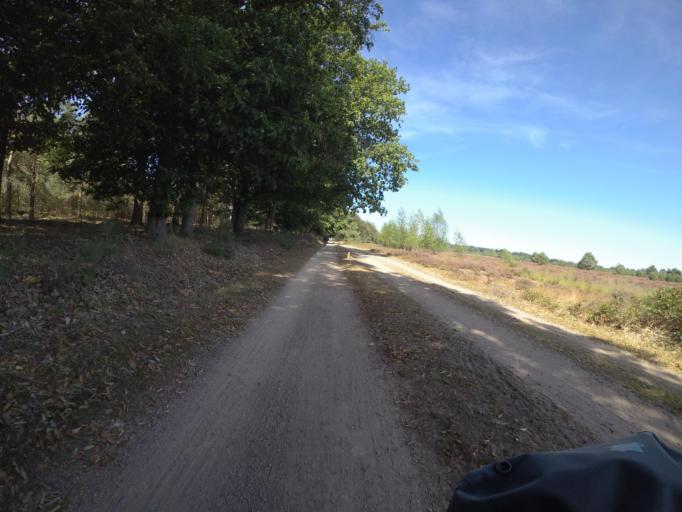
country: NL
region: Overijssel
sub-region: Gemeente Raalte
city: Raalte
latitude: 52.3317
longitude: 6.3881
